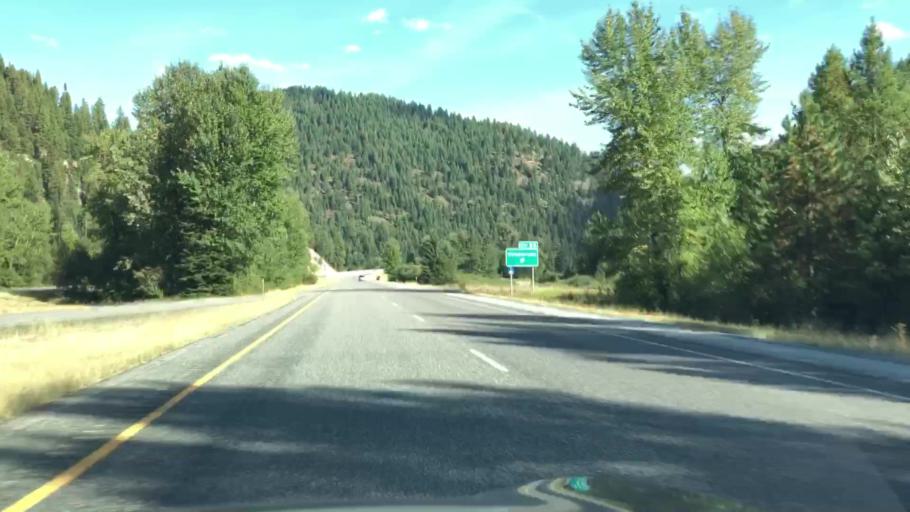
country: US
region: Montana
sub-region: Sanders County
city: Thompson Falls
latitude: 47.3570
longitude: -115.3025
